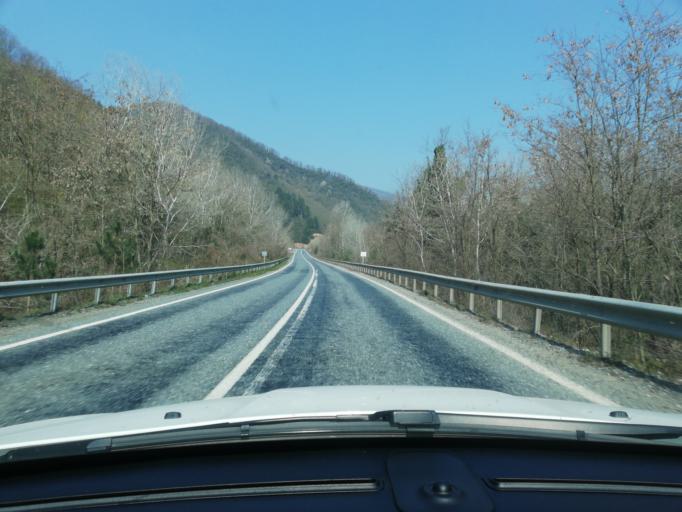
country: TR
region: Zonguldak
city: Gokcebey
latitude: 41.2452
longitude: 32.1686
